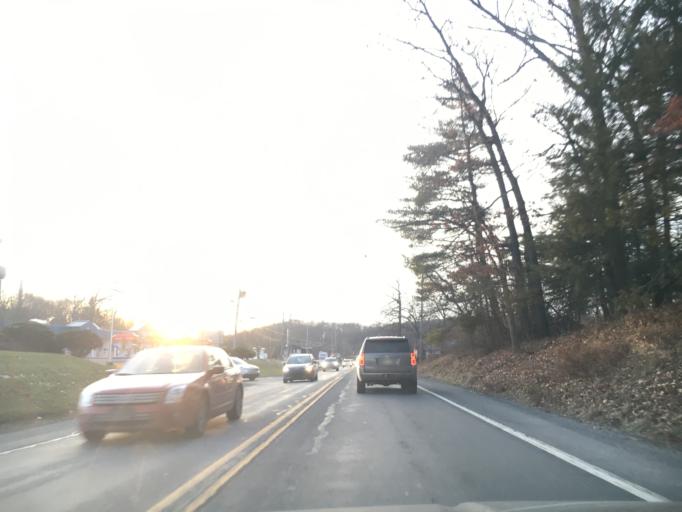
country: US
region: Pennsylvania
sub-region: Monroe County
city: East Stroudsburg
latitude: 41.0034
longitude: -75.1463
